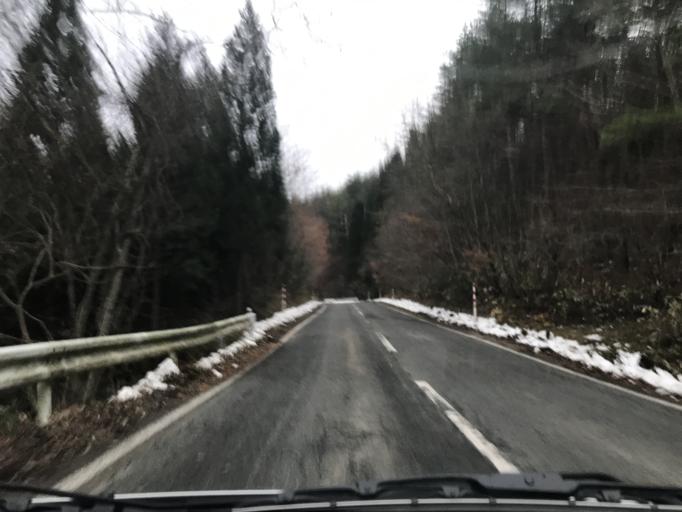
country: JP
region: Iwate
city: Mizusawa
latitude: 39.1417
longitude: 141.3658
